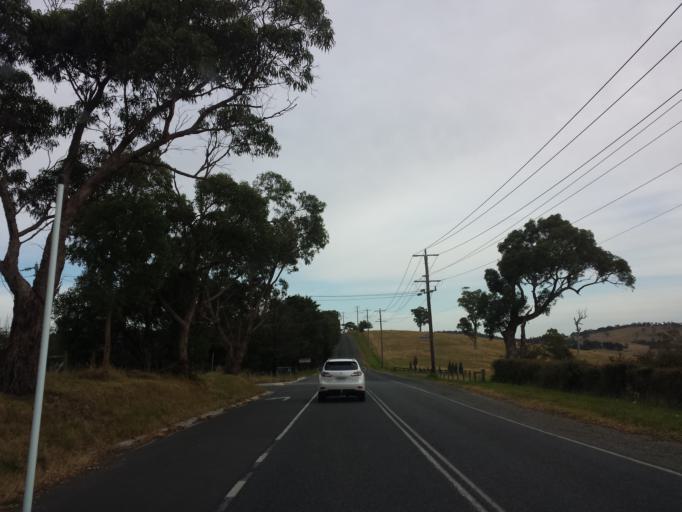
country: AU
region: Victoria
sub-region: Knox
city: Ferntree Gully
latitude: -37.9053
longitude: 145.3047
